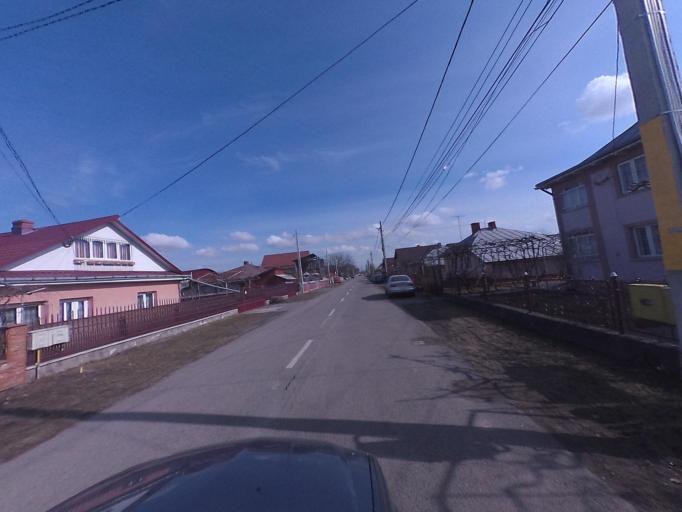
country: RO
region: Neamt
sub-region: Oras Targu Neamt
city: Targu Neamt
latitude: 47.2052
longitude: 26.3787
